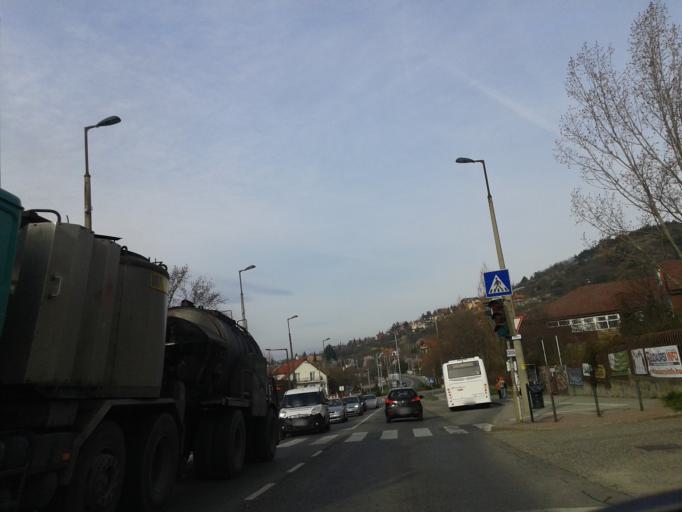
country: HU
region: Pest
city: Budaors
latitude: 47.4606
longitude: 18.9408
